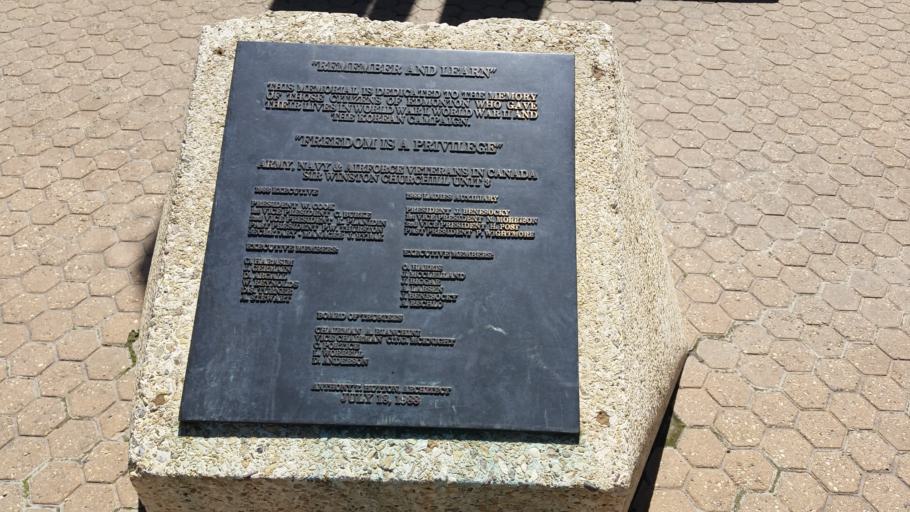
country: CA
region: Alberta
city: Edmonton
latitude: 53.5415
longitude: -113.4868
